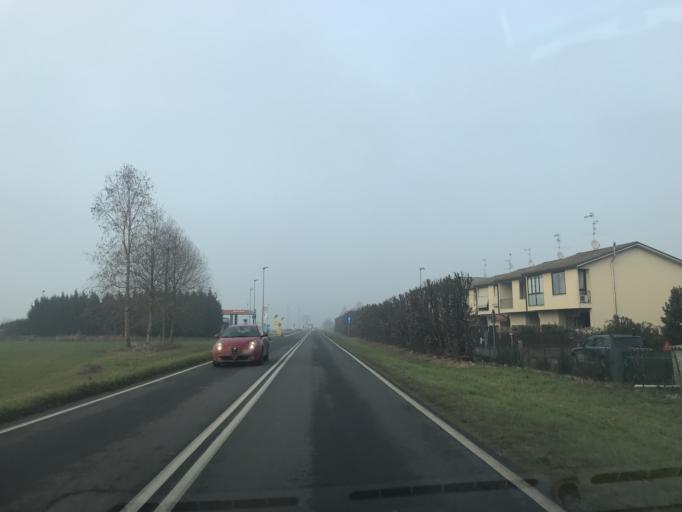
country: IT
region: Lombardy
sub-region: Provincia di Lodi
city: Ossago Lodigiano
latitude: 45.2461
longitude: 9.5355
